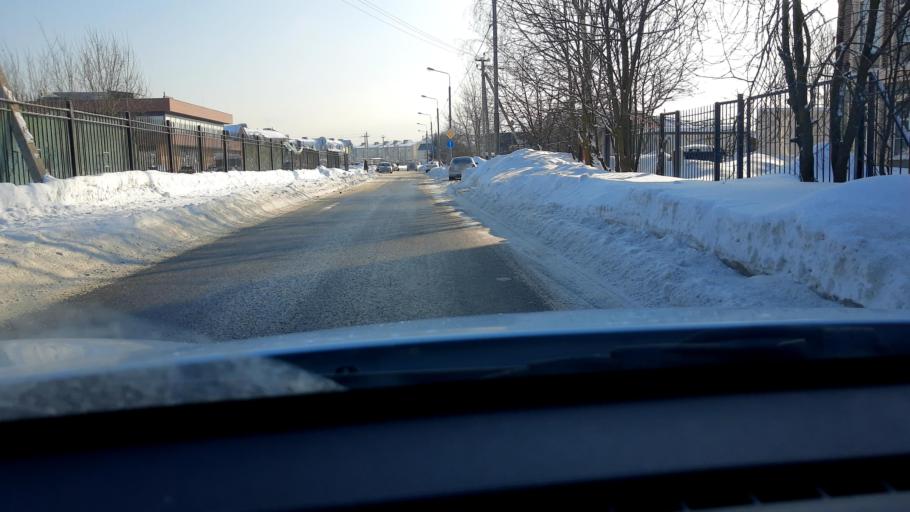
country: RU
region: Moskovskaya
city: Vatutinki
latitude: 55.4959
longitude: 37.3197
